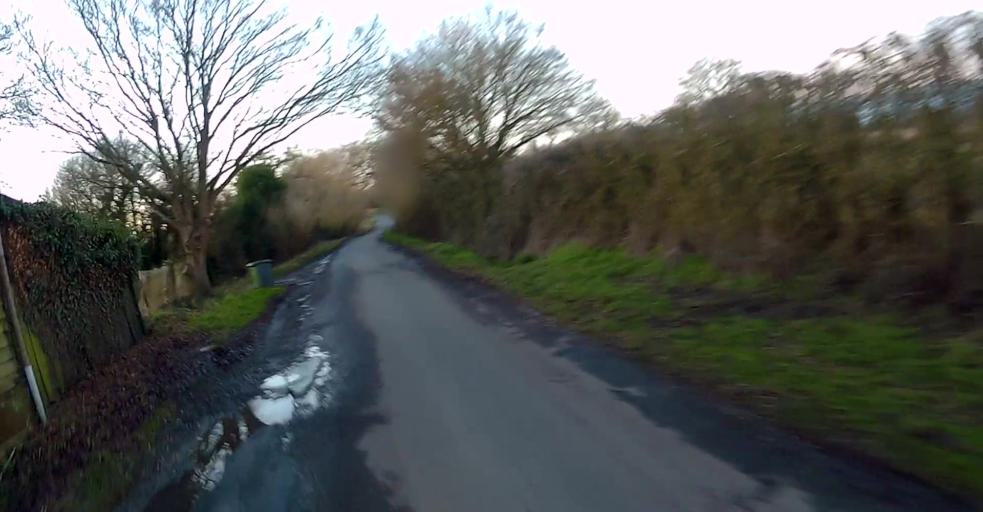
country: GB
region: England
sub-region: West Berkshire
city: Stratfield Mortimer
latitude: 51.3355
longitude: -1.0548
